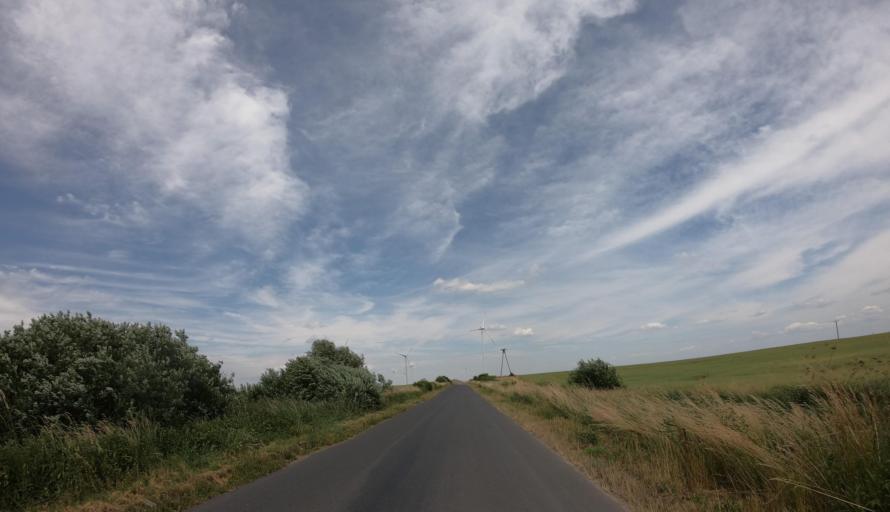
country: PL
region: West Pomeranian Voivodeship
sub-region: Powiat pyrzycki
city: Kozielice
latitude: 53.0845
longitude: 14.8309
